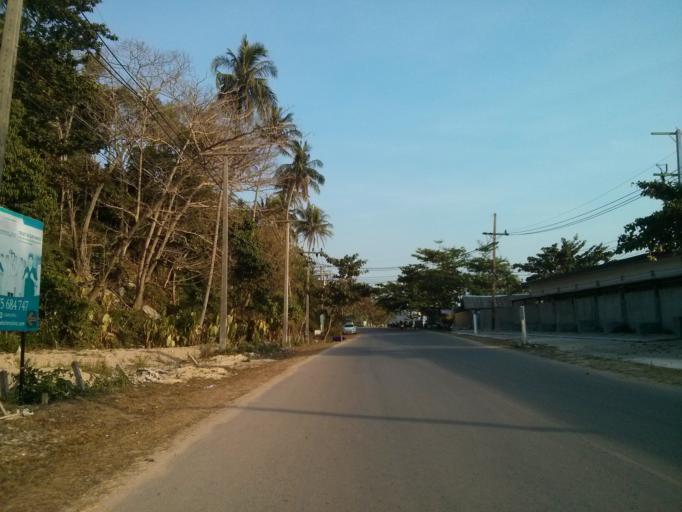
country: TH
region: Krabi
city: Ko Lanta
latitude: 7.5553
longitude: 99.0399
